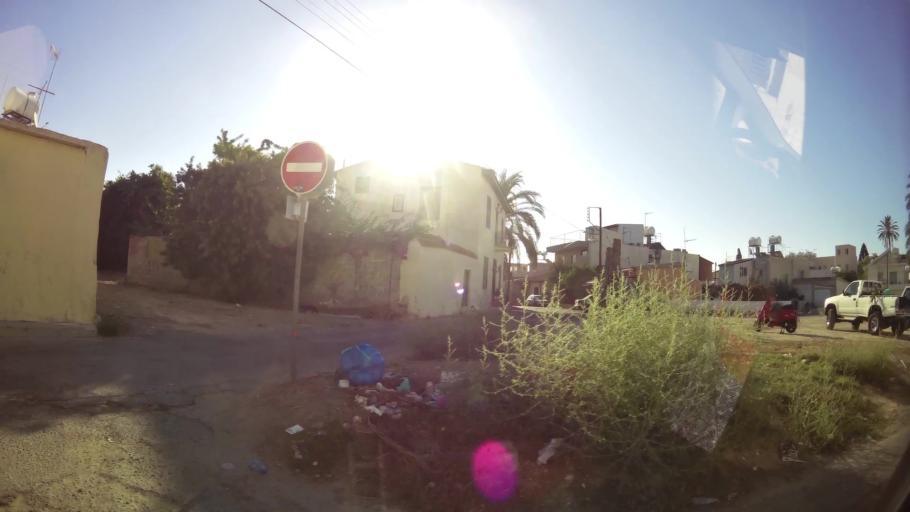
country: CY
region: Larnaka
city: Larnaca
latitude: 34.9237
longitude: 33.6241
